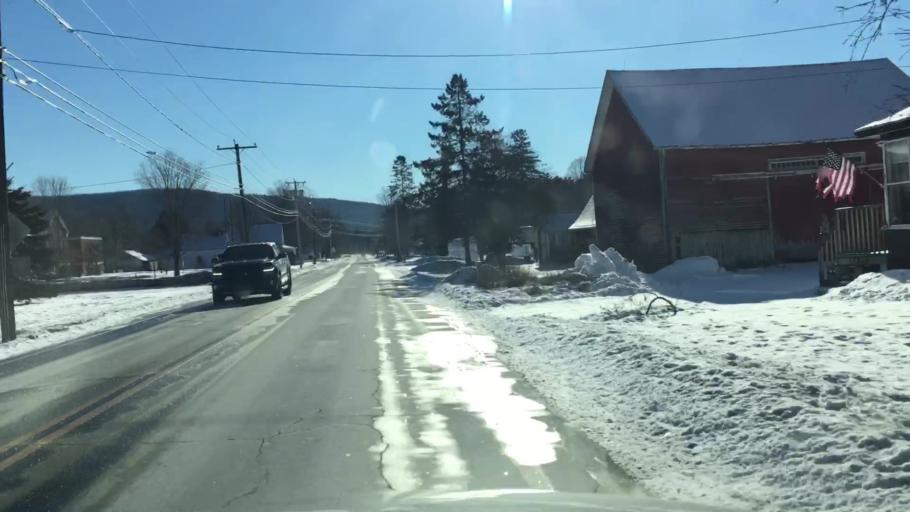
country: US
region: New Hampshire
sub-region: Grafton County
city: Woodsville
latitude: 44.2593
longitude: -72.0532
